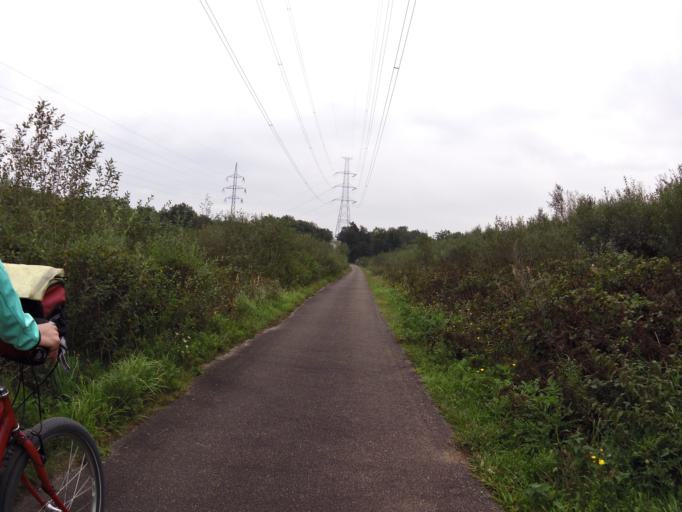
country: BE
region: Flanders
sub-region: Provincie Limburg
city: As
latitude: 51.0025
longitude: 5.6032
